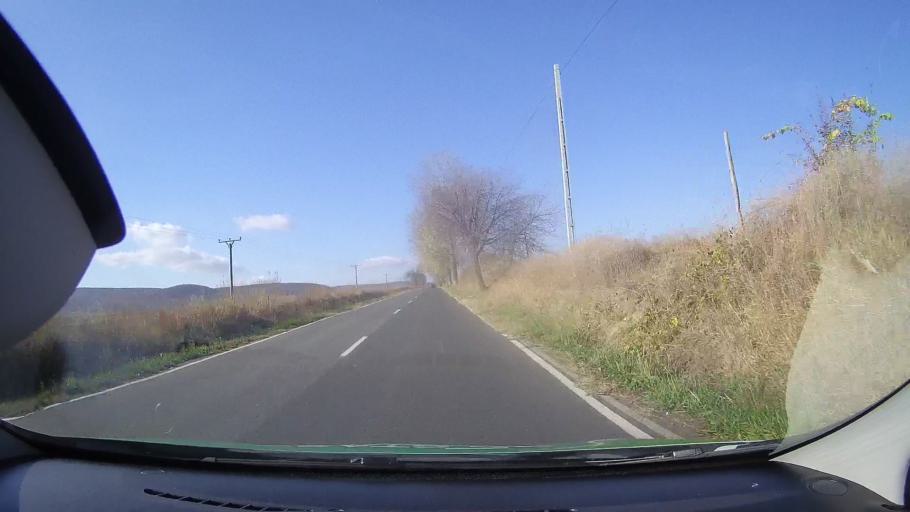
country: RO
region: Tulcea
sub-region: Comuna Sarichioi
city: Enisala
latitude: 44.8792
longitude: 28.7871
